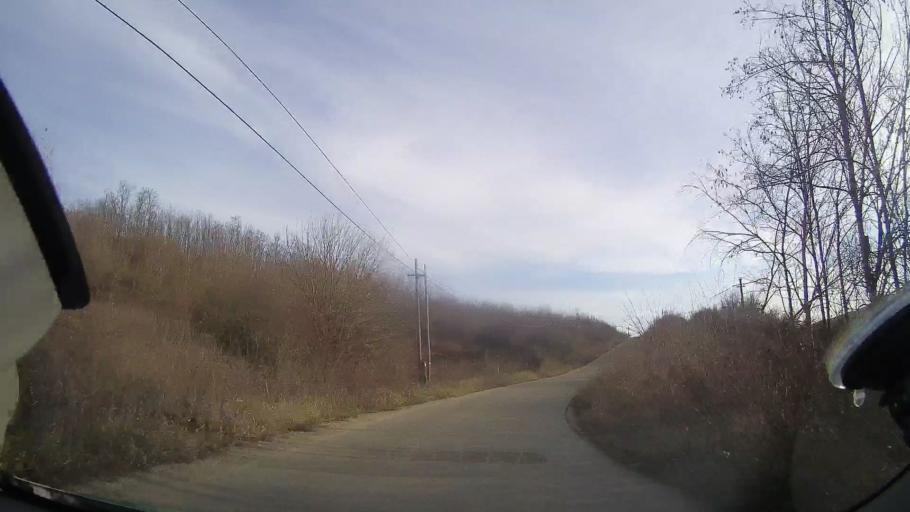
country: RO
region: Bihor
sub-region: Comuna Sarbi
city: Sarbi
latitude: 47.1869
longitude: 22.1278
